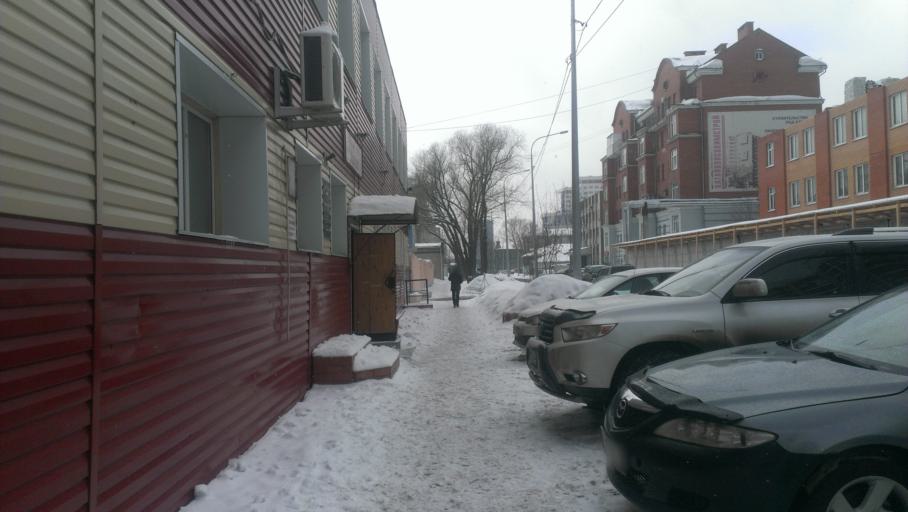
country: RU
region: Altai Krai
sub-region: Gorod Barnaulskiy
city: Barnaul
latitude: 53.3331
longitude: 83.7864
